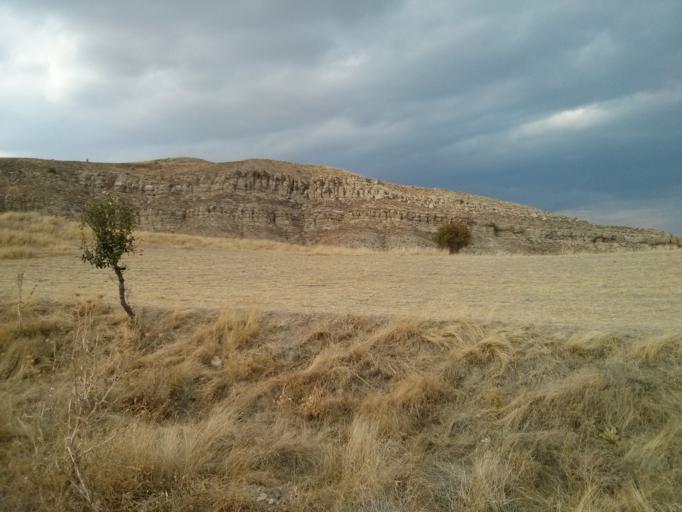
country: TR
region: Ankara
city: Hasayaz
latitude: 40.2797
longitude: 33.2977
